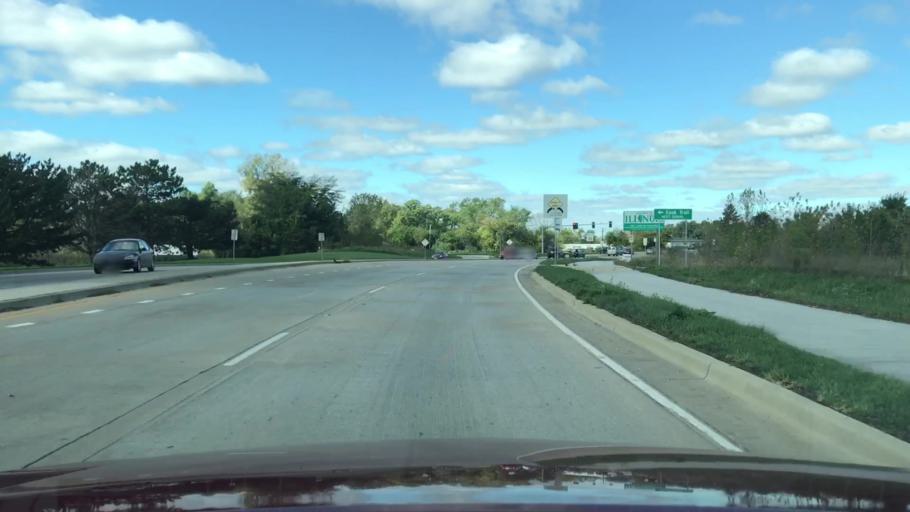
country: US
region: Indiana
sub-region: Lake County
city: Dyer
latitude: 41.4949
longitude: -87.5260
